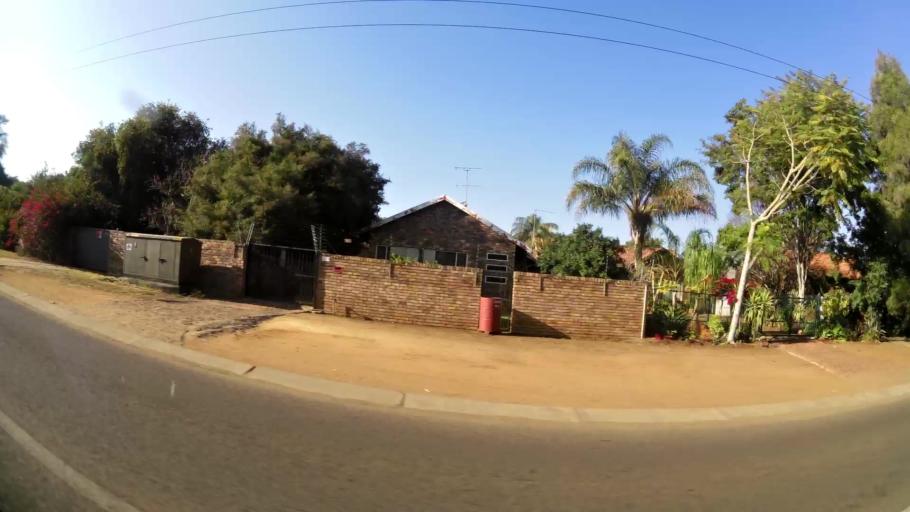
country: ZA
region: Gauteng
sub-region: City of Tshwane Metropolitan Municipality
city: Pretoria
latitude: -25.6730
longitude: 28.2130
